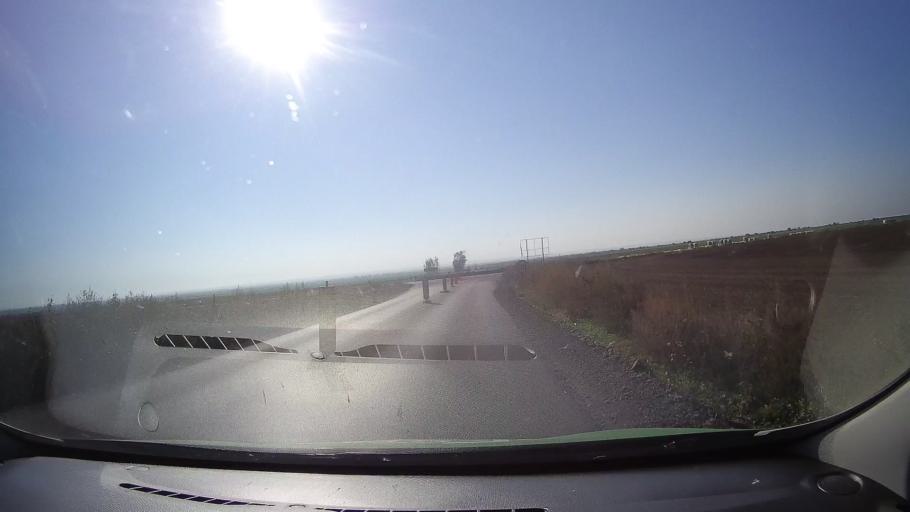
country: RO
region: Satu Mare
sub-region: Comuna Tiream
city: Tiream
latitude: 47.6437
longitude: 22.4643
